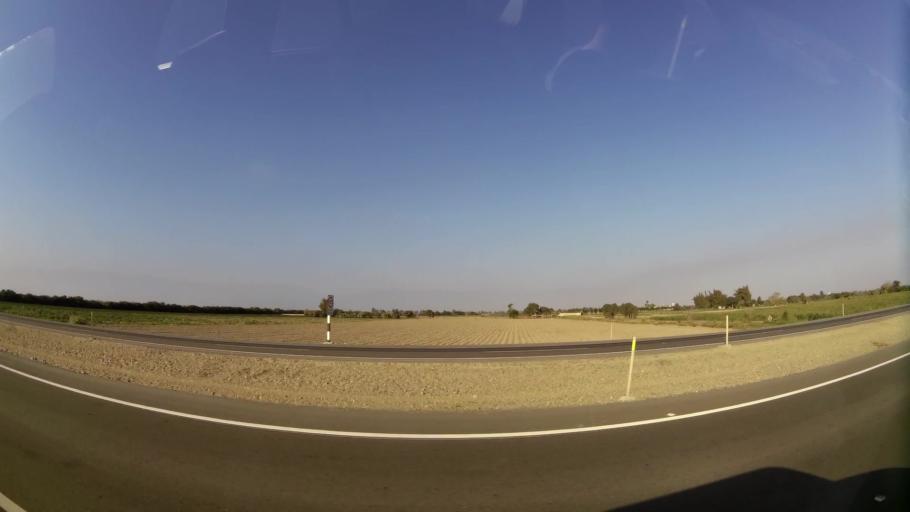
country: PE
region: Ica
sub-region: Provincia de Chincha
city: Chincha Baja
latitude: -13.5148
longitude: -76.1842
